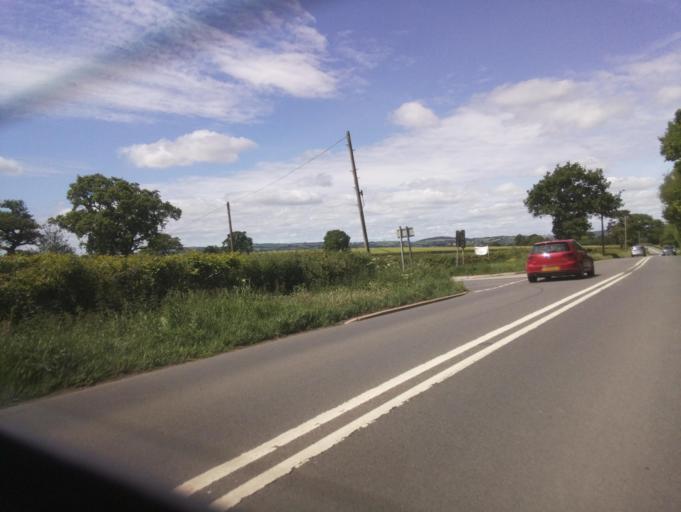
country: GB
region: England
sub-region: Devon
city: Cullompton
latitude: 50.8553
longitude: -3.3403
